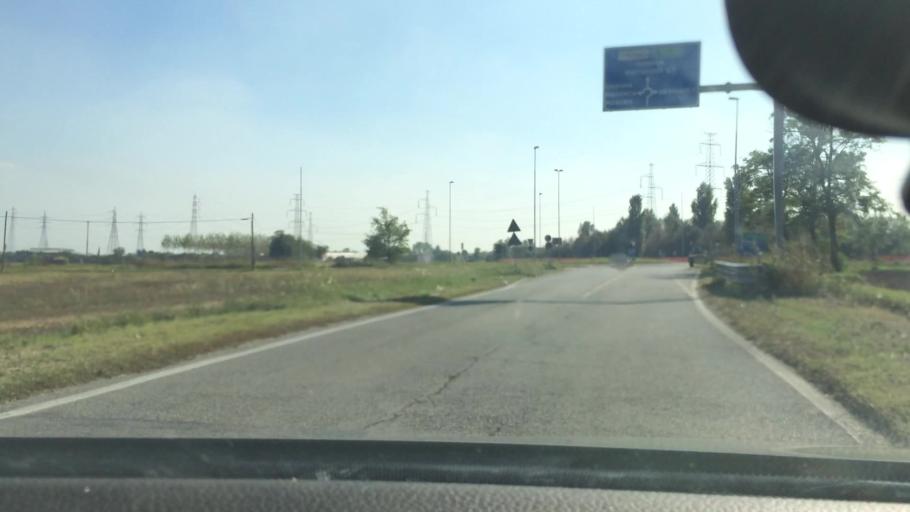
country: IT
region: Lombardy
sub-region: Citta metropolitana di Milano
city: Casate
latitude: 45.4870
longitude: 8.8291
